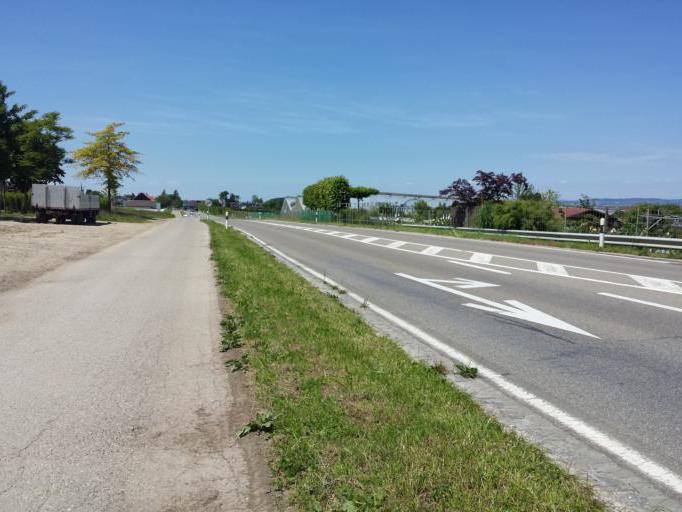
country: CH
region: Thurgau
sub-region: Arbon District
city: Uttwil
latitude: 47.5893
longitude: 9.3279
